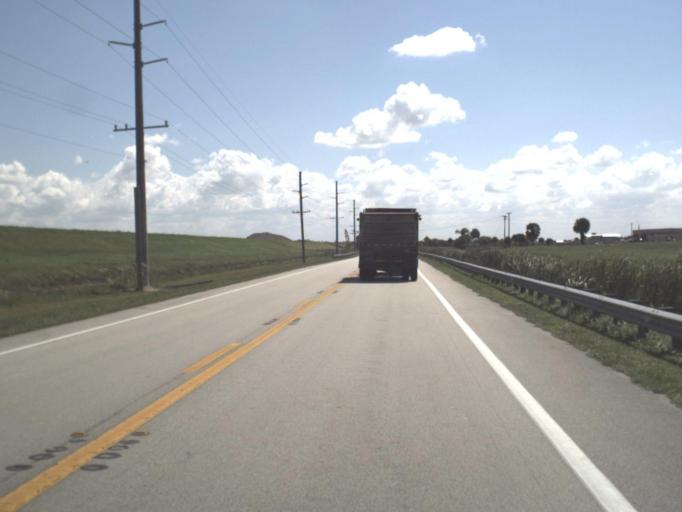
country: US
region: Florida
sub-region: Glades County
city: Moore Haven
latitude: 26.8937
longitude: -81.1226
